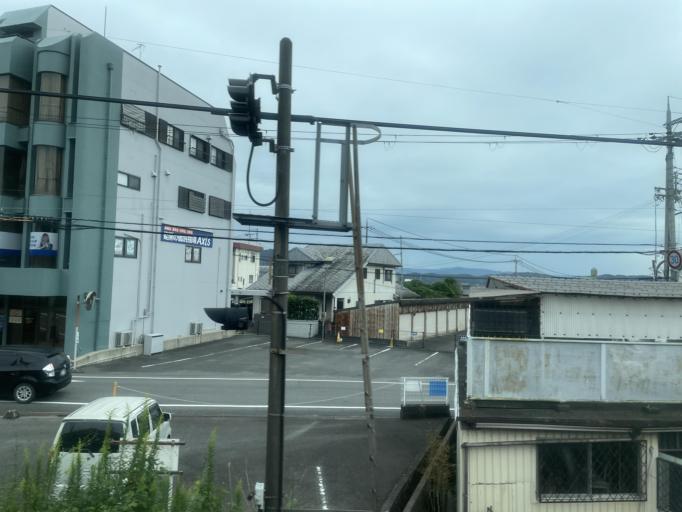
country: JP
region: Wakayama
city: Iwade
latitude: 34.2696
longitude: 135.2492
